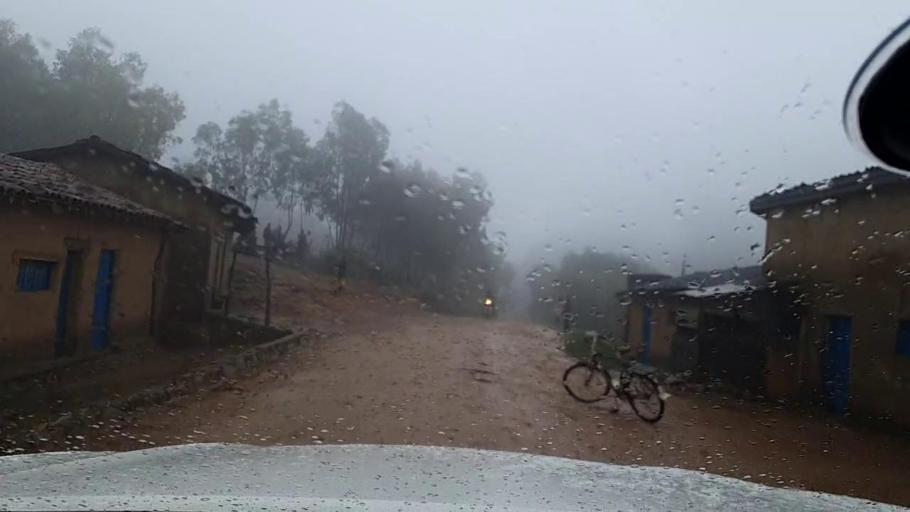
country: RW
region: Western Province
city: Kibuye
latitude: -2.1368
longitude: 29.4659
